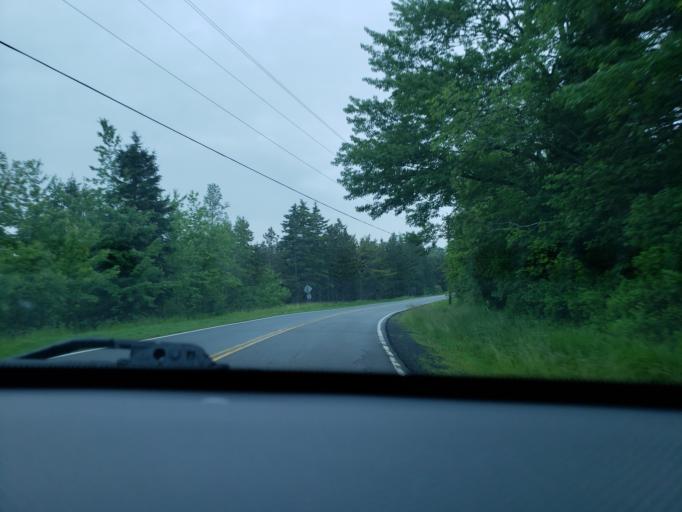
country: CA
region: Nova Scotia
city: Windsor
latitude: 45.0604
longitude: -63.9828
